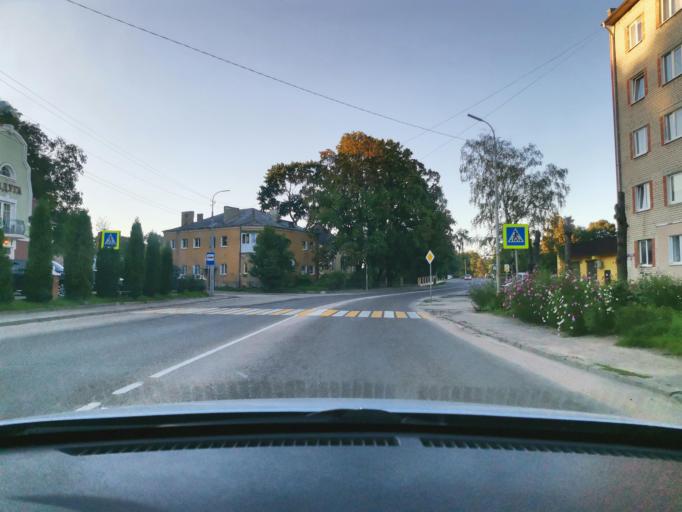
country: RU
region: Kaliningrad
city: Chernyakhovsk
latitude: 54.6413
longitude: 21.8075
